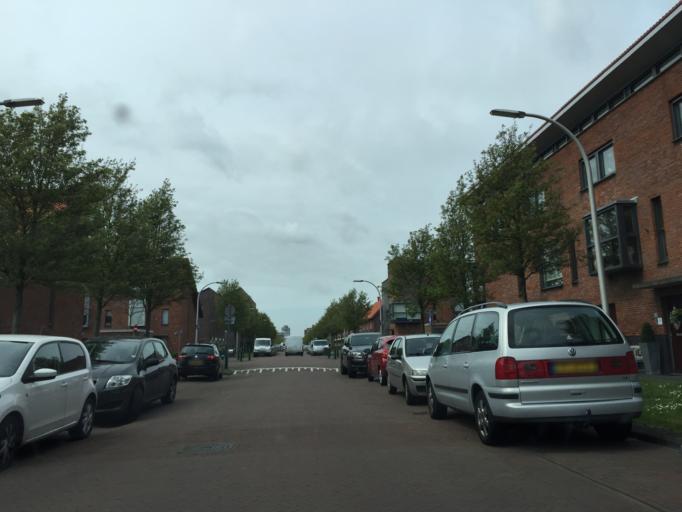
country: NL
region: South Holland
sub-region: Gemeente Den Haag
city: Ypenburg
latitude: 52.0371
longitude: 4.3641
